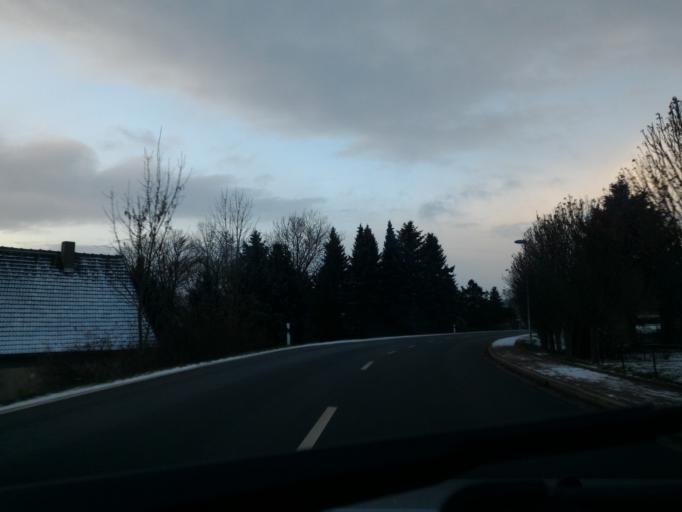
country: DE
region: Saxony
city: Leutersdorf
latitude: 50.9527
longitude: 14.6502
